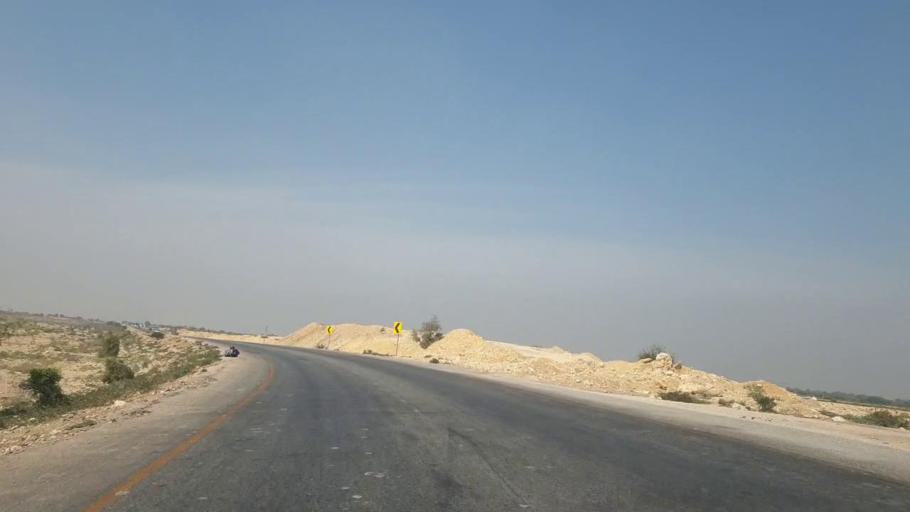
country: PK
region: Sindh
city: Hala
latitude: 25.8643
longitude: 68.2598
